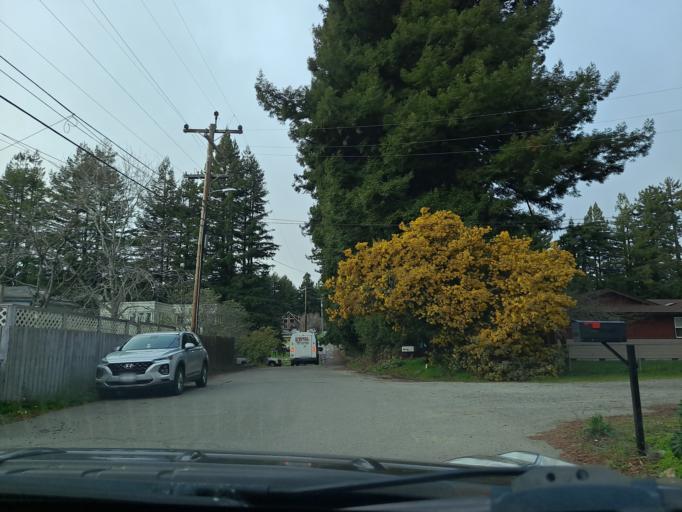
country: US
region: California
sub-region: Humboldt County
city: Fortuna
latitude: 40.6055
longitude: -124.1543
